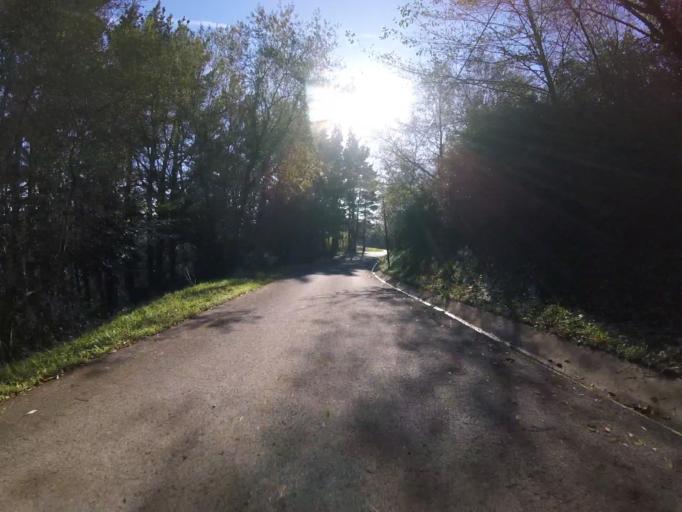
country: ES
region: Basque Country
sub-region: Provincia de Guipuzcoa
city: Usurbil
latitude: 43.2928
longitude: -2.0384
